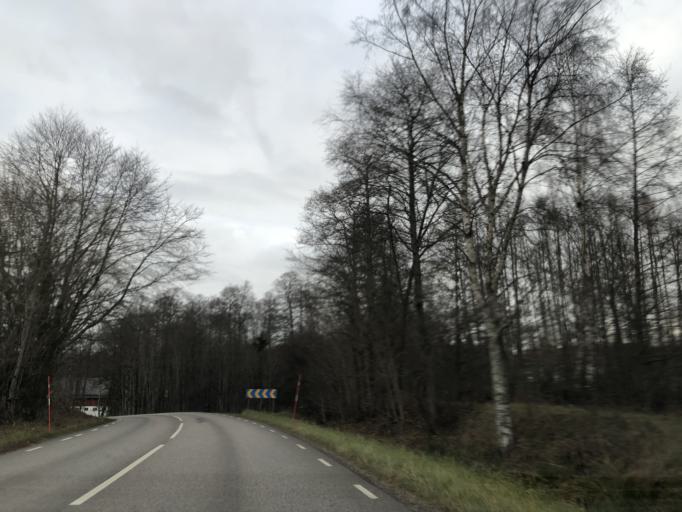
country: SE
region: Vaestra Goetaland
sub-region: Ulricehamns Kommun
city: Ulricehamn
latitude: 57.6781
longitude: 13.3995
